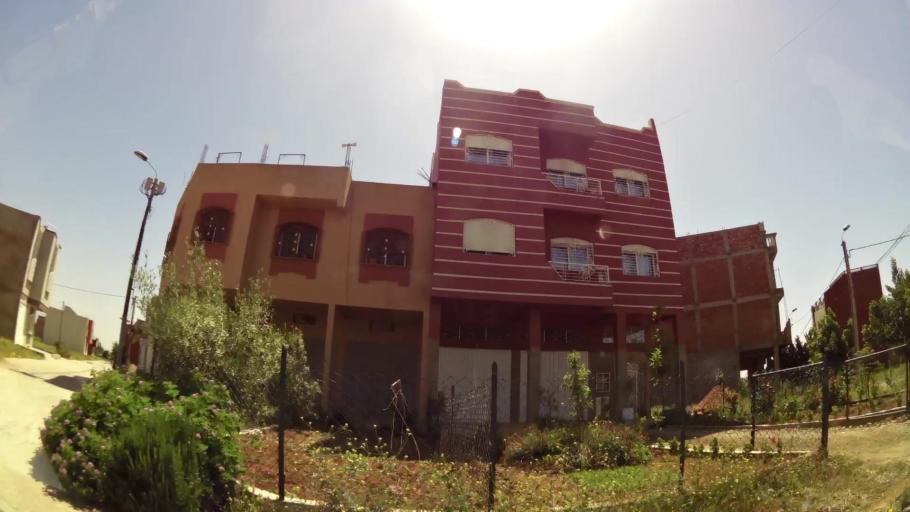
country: MA
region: Rabat-Sale-Zemmour-Zaer
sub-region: Khemisset
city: Khemisset
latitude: 33.8104
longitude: -6.0901
